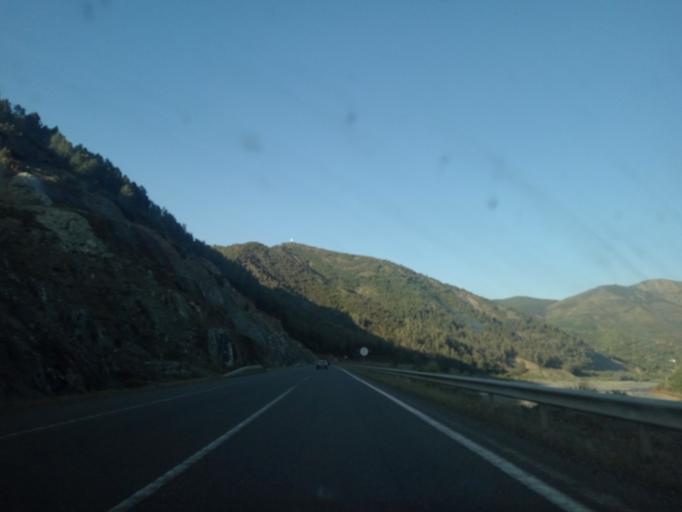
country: AL
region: Lezhe
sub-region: Rrethi i Mirdites
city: Rubik
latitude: 41.7897
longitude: 19.7986
